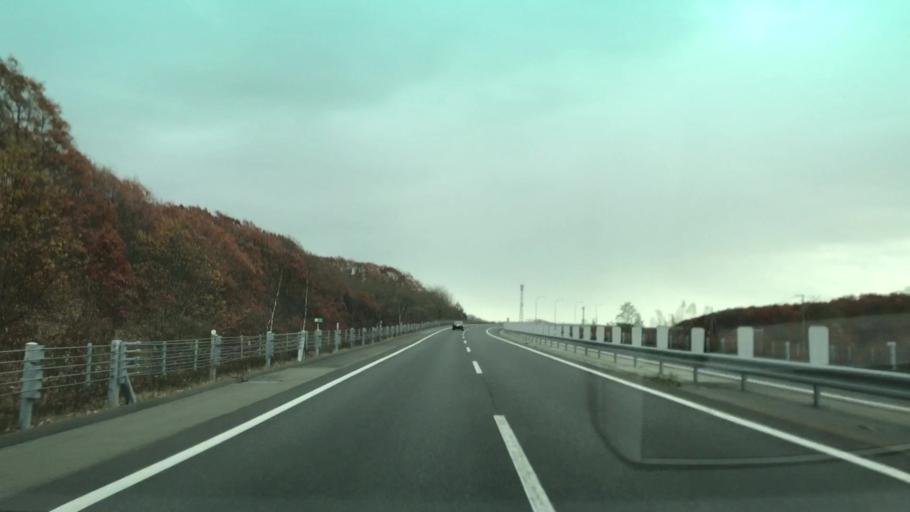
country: JP
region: Hokkaido
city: Tomakomai
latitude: 42.6575
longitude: 141.8252
